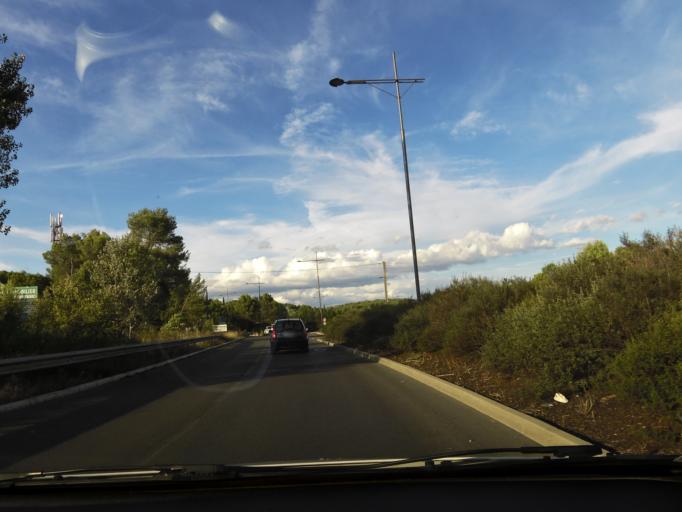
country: FR
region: Languedoc-Roussillon
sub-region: Departement de l'Herault
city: Clapiers
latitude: 43.6537
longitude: 3.8735
